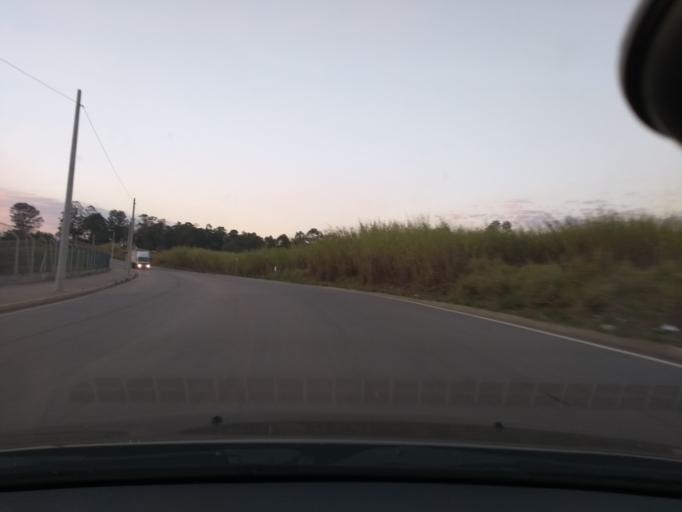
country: BR
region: Sao Paulo
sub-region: Louveira
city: Louveira
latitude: -23.1174
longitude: -47.0034
